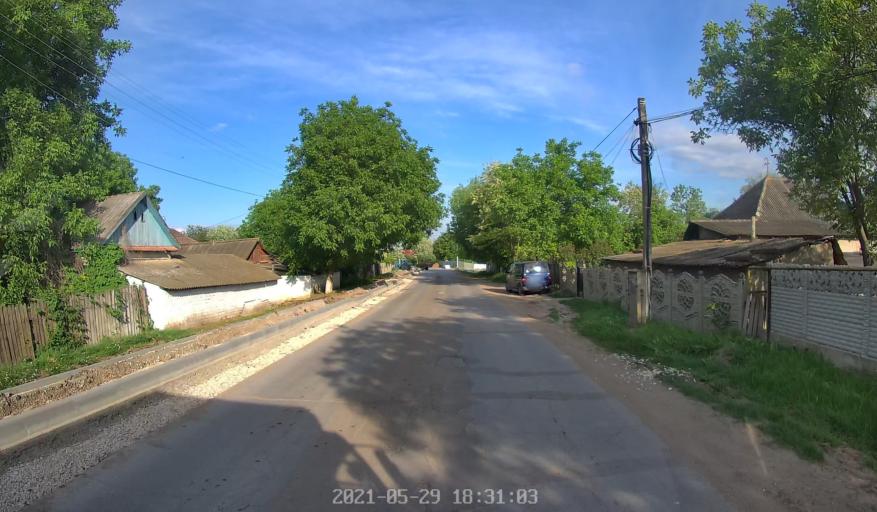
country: MD
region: Chisinau
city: Singera
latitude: 46.8208
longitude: 28.8812
